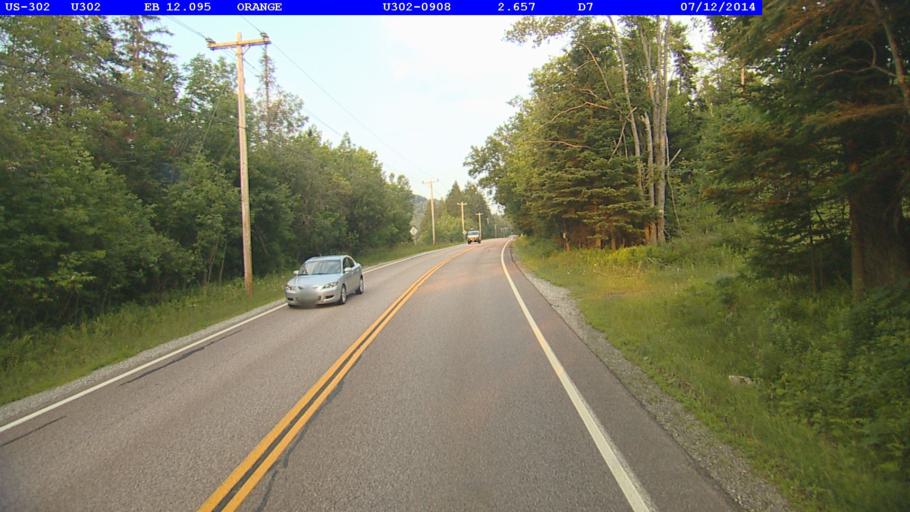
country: US
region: Vermont
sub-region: Washington County
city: South Barre
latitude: 44.1469
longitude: -72.3865
